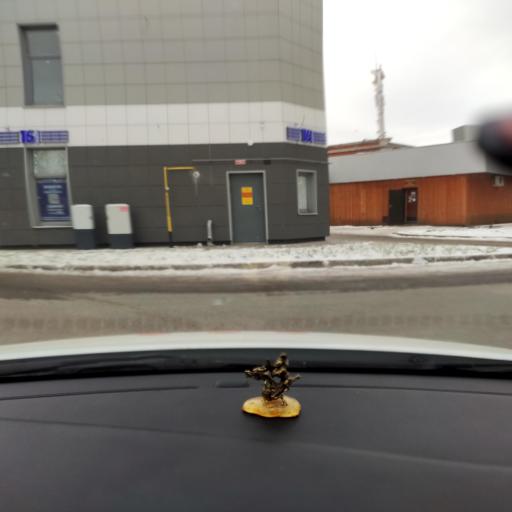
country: RU
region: Tatarstan
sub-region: Zelenodol'skiy Rayon
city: Zelenodolsk
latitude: 55.8508
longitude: 48.5020
